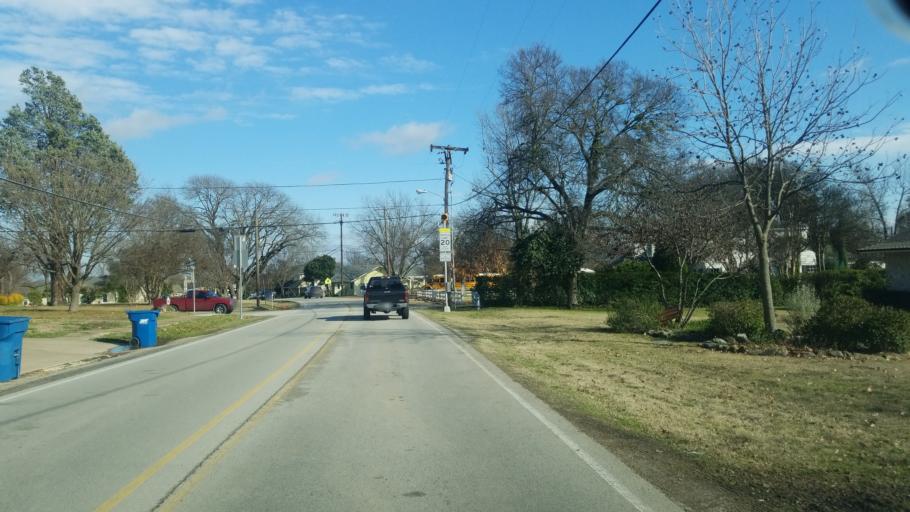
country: US
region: Texas
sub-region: Rockwall County
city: Rockwall
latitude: 32.9336
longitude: -96.4558
